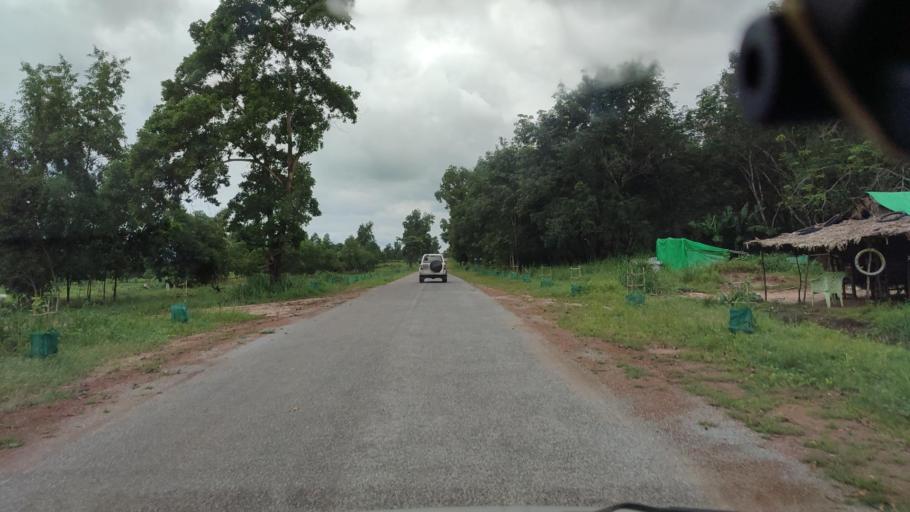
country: MM
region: Bago
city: Thanatpin
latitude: 17.2485
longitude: 96.3314
